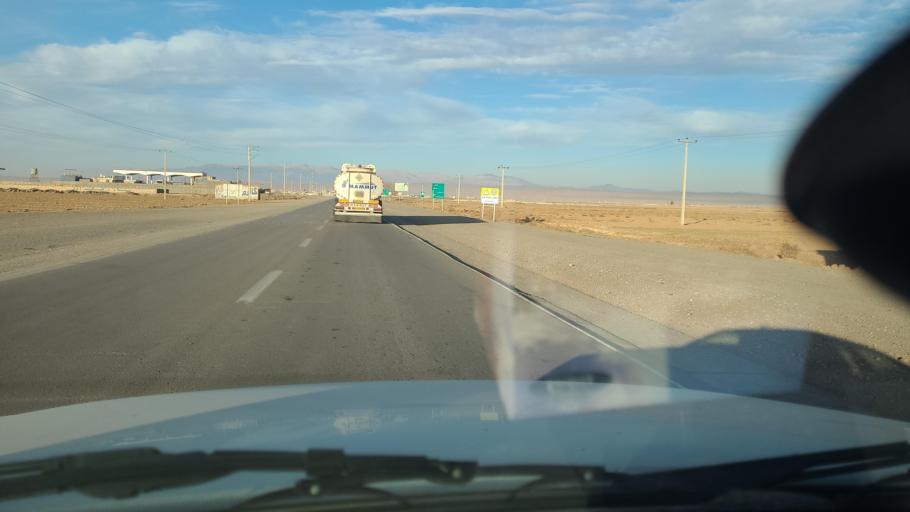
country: IR
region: Razavi Khorasan
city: Neqab
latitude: 36.6079
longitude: 57.5926
